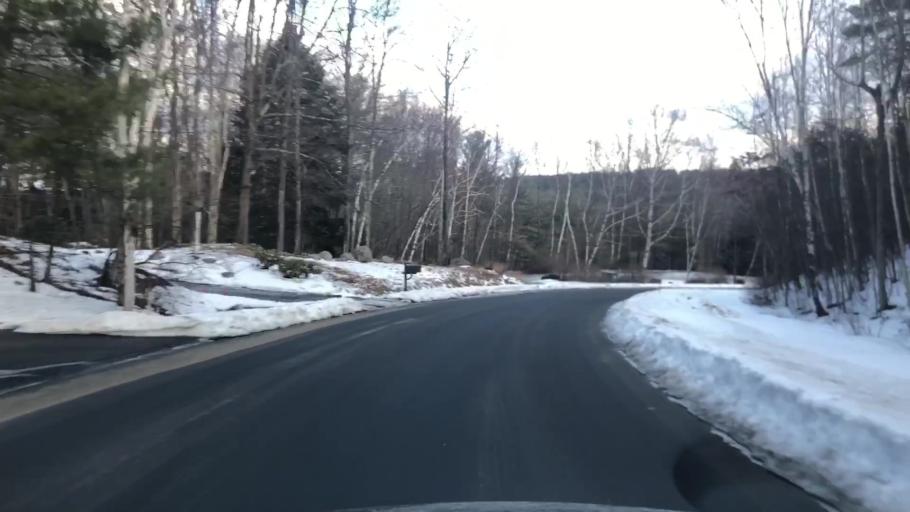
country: US
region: New Hampshire
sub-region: Hillsborough County
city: Milford
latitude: 42.8520
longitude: -71.6215
